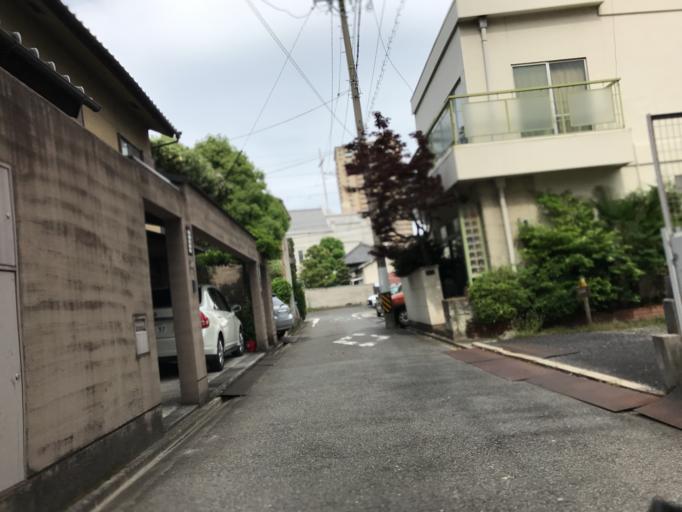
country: JP
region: Aichi
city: Nagoya-shi
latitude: 35.1682
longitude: 136.9327
